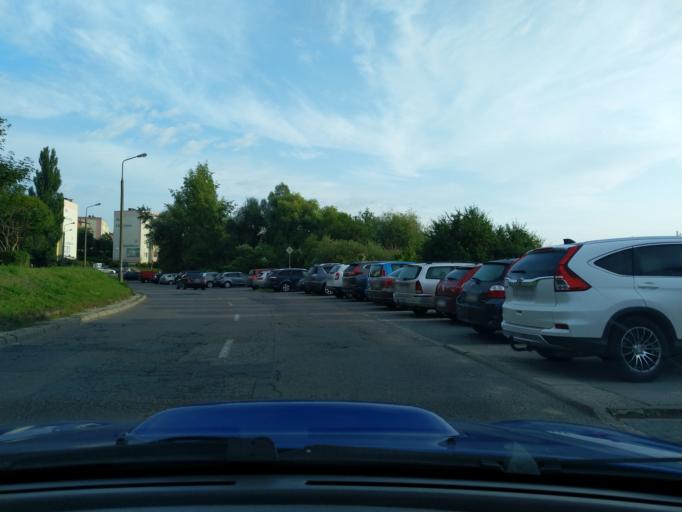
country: PL
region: Warmian-Masurian Voivodeship
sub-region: Olsztyn
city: Kortowo
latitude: 53.7598
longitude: 20.4718
